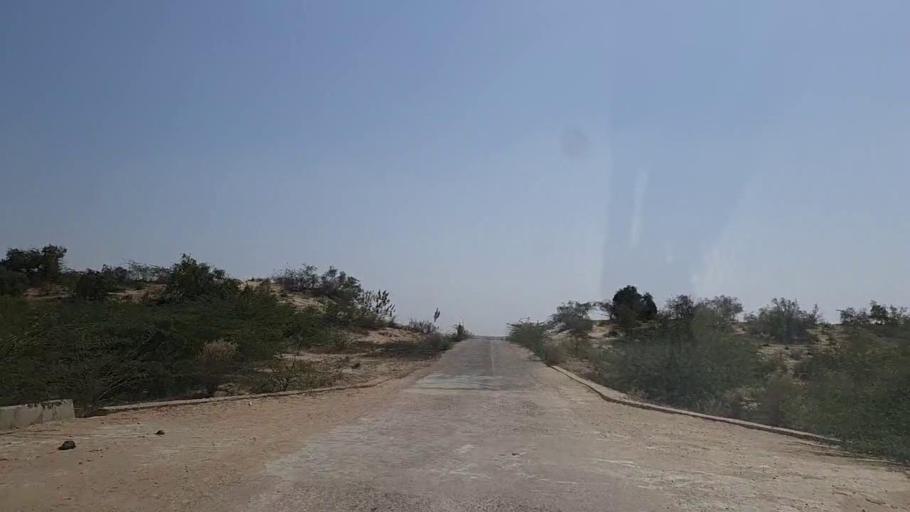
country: PK
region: Sindh
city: Diplo
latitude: 24.5006
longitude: 69.4286
